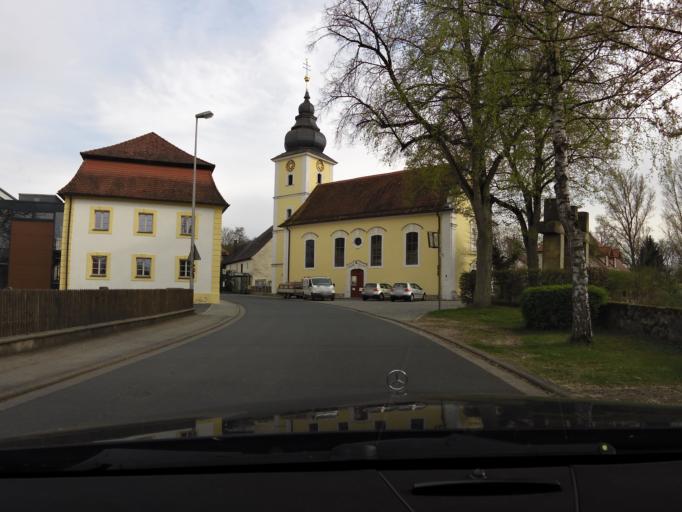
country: DE
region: Bavaria
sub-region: Upper Franconia
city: Pommersfelden
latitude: 49.7676
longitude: 10.8182
